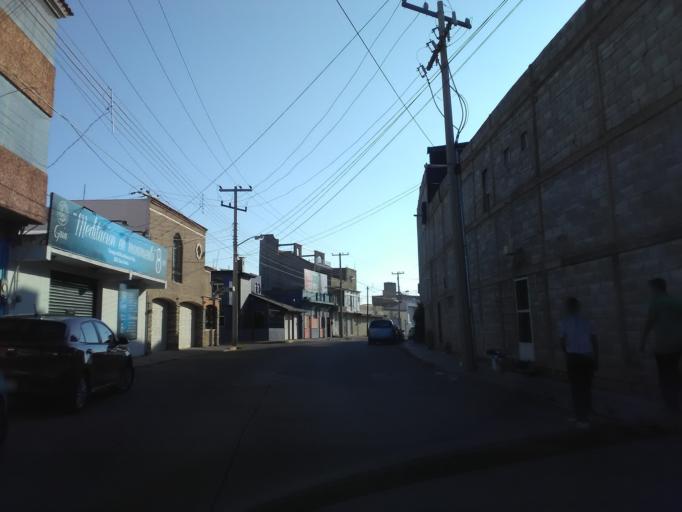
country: MX
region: Durango
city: Victoria de Durango
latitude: 24.0408
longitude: -104.6323
